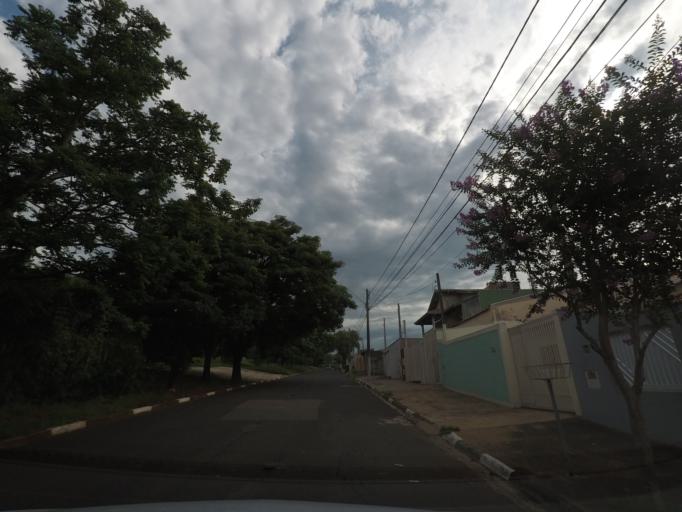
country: BR
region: Sao Paulo
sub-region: Campinas
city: Campinas
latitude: -22.8861
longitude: -47.1288
